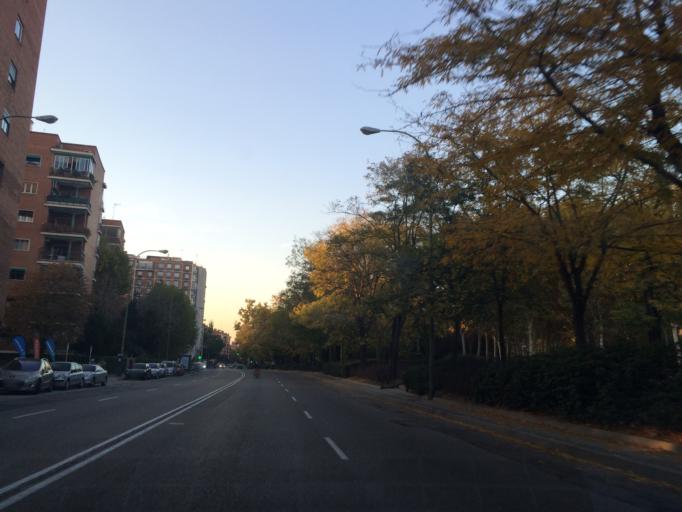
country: ES
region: Madrid
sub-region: Provincia de Madrid
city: Moncloa-Aravaca
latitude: 40.4270
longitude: -3.7278
